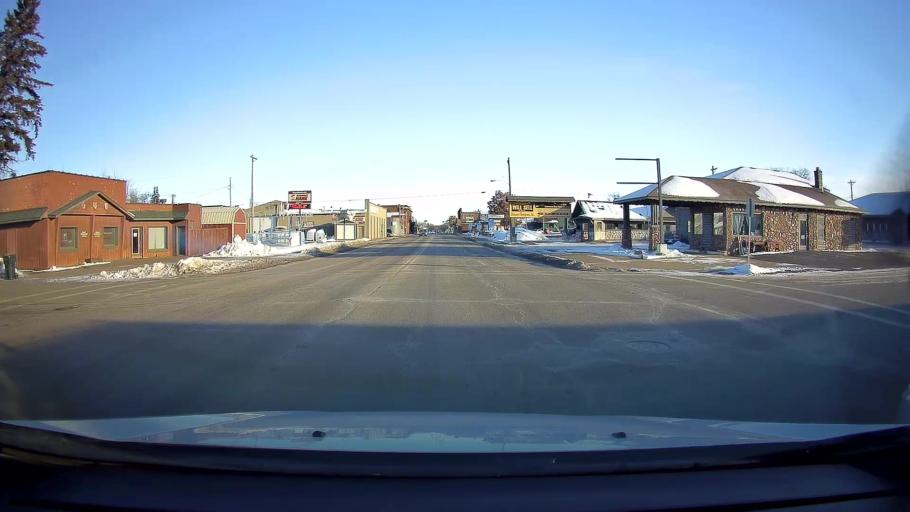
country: US
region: Wisconsin
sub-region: Washburn County
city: Spooner
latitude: 45.8247
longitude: -91.8897
